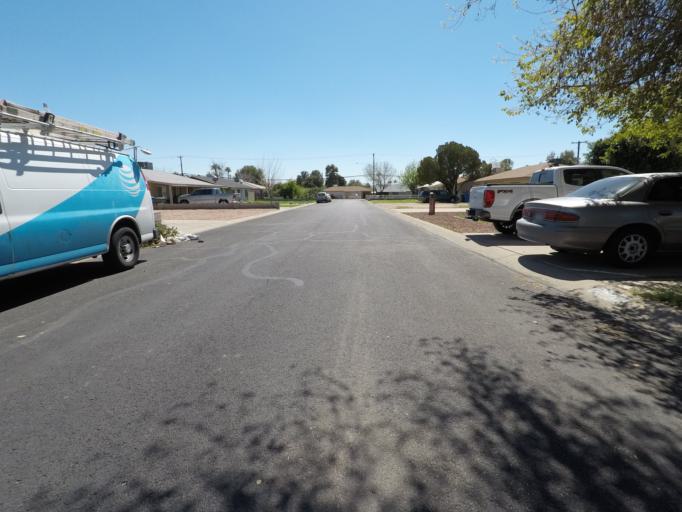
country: US
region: Arizona
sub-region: Maricopa County
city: Phoenix
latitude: 33.4795
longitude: -112.0113
